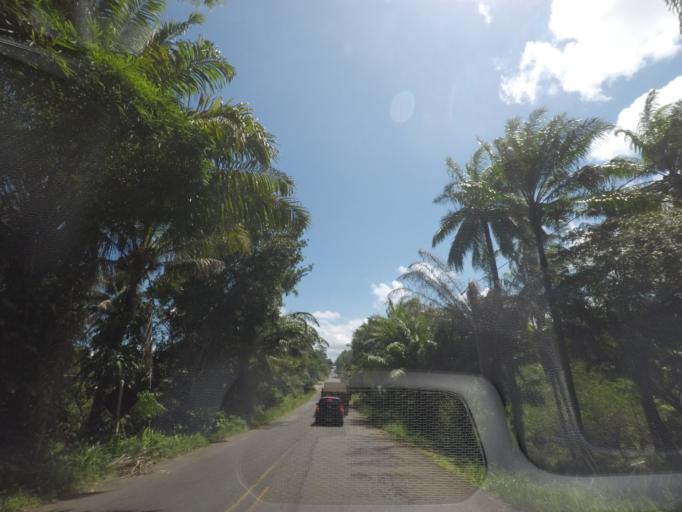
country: BR
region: Bahia
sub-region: Valenca
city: Valenca
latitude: -13.4485
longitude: -39.0852
